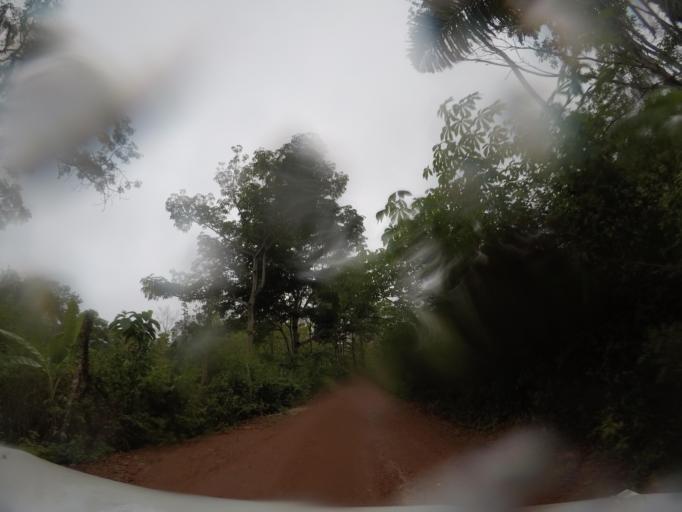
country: TL
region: Baucau
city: Venilale
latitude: -8.6296
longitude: 126.4295
